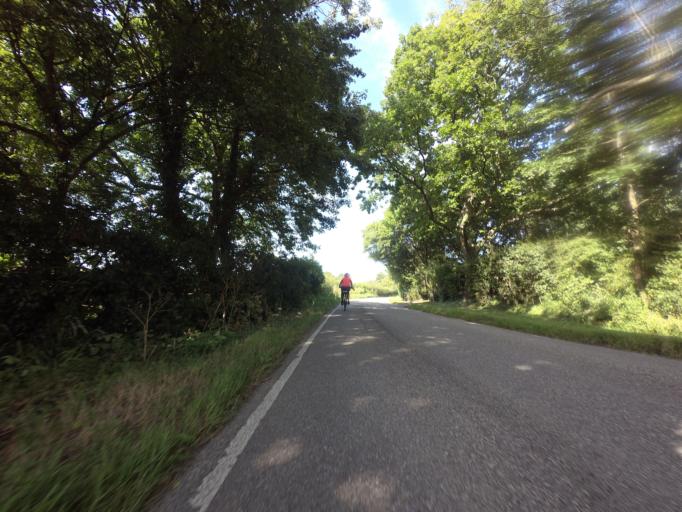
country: GB
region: England
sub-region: Kent
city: Tenterden
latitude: 51.0091
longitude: 0.7004
